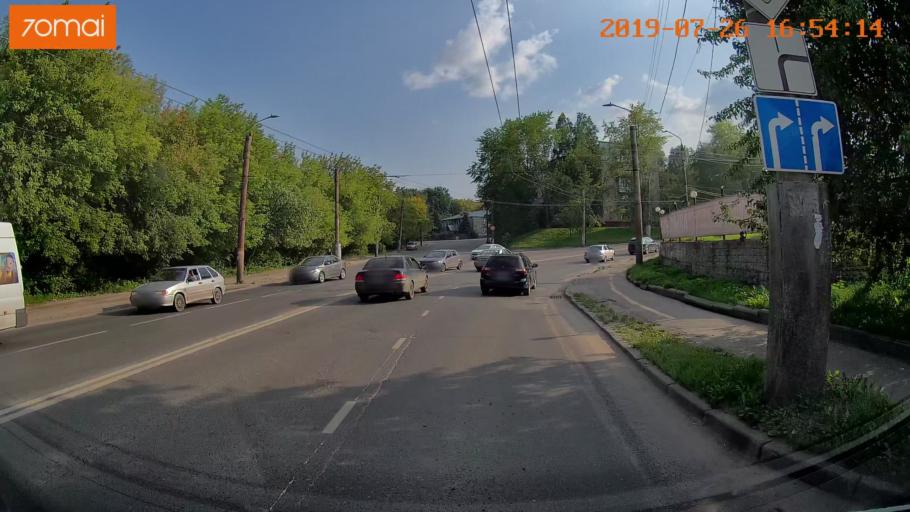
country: RU
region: Ivanovo
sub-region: Gorod Ivanovo
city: Ivanovo
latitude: 57.0116
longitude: 41.0009
